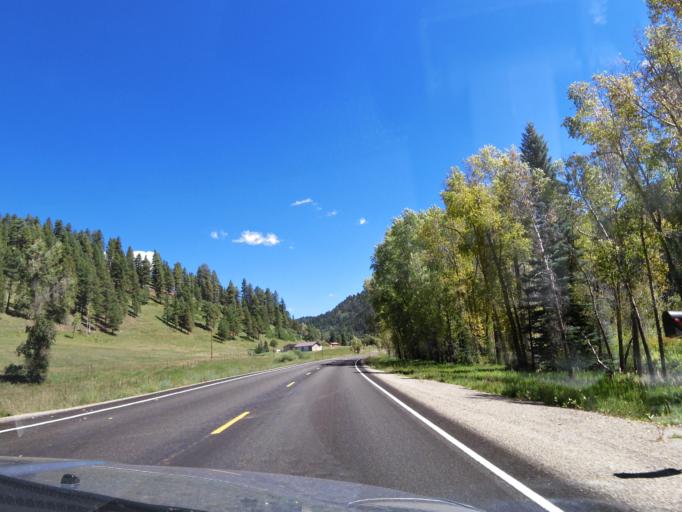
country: US
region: Colorado
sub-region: Montezuma County
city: Mancos
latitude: 37.6079
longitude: -108.0974
